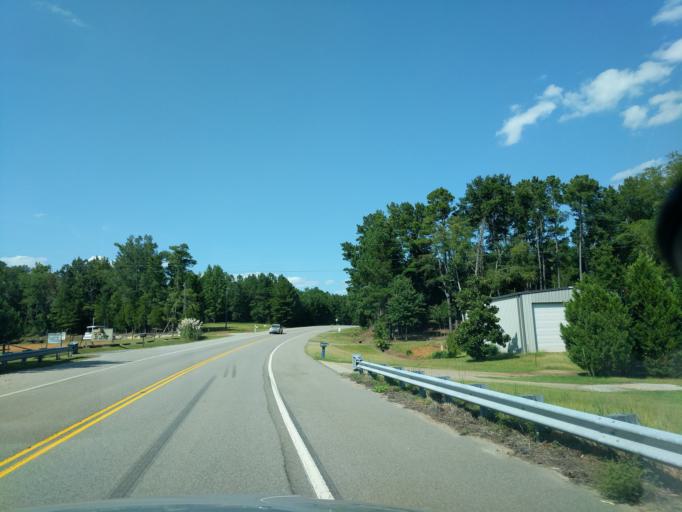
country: US
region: South Carolina
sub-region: Newberry County
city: Prosperity
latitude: 34.1014
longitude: -81.5685
